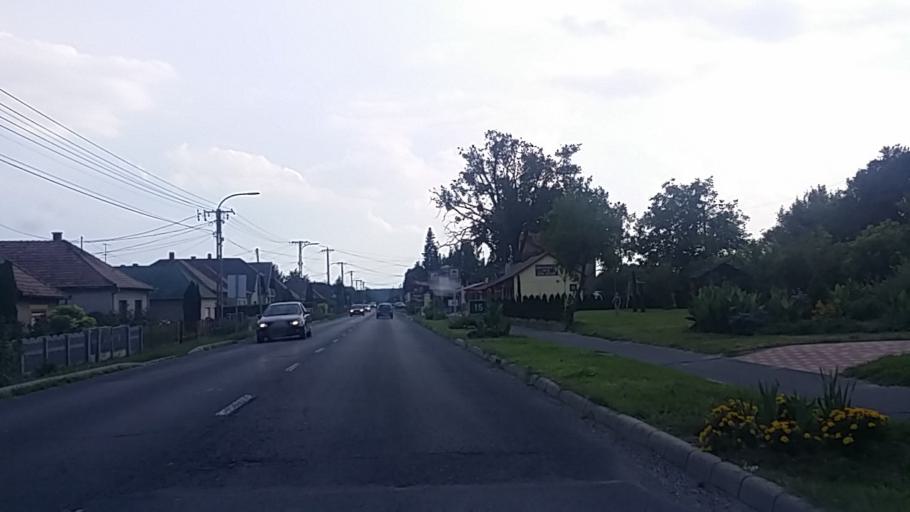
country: HU
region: Zala
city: Sarmellek
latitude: 46.7110
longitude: 17.1692
